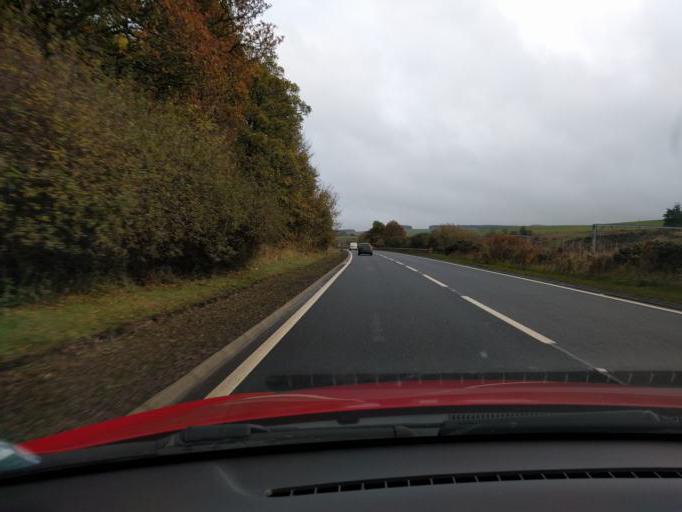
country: GB
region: Scotland
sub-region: The Scottish Borders
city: Duns
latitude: 55.8847
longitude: -2.3160
